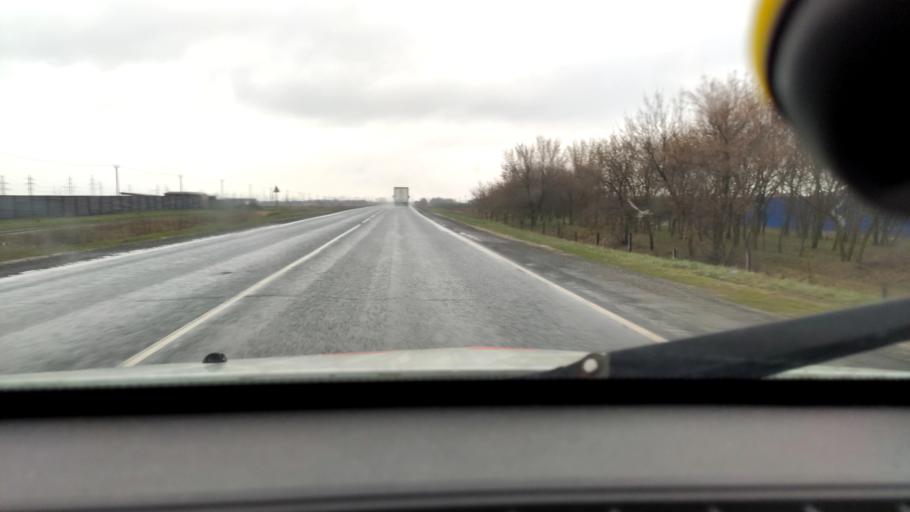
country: RU
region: Samara
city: Povolzhskiy
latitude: 53.6436
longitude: 49.6670
